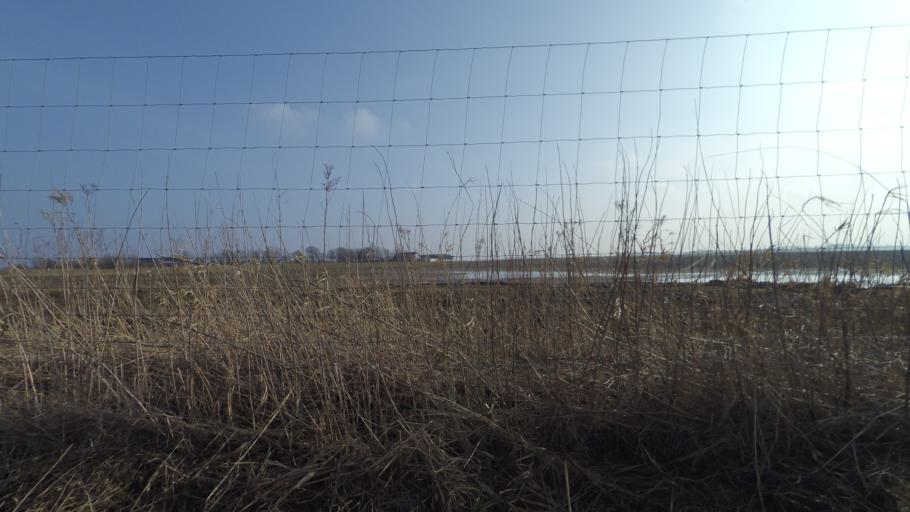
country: DK
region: Central Jutland
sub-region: Arhus Kommune
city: Tranbjerg
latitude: 56.0798
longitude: 10.1378
